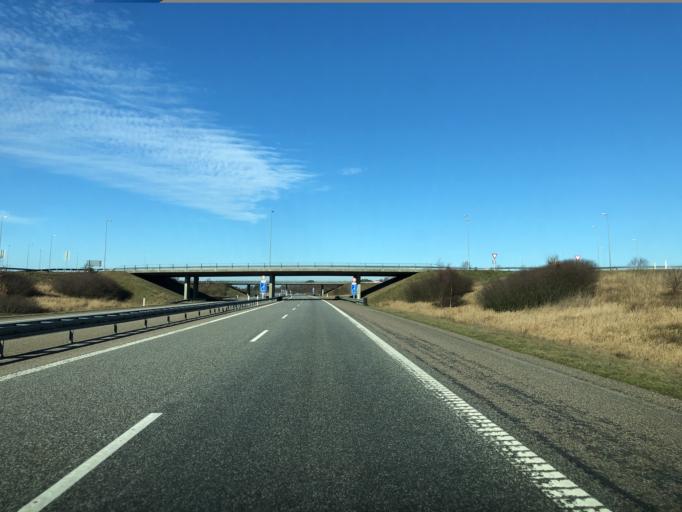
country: DK
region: Central Jutland
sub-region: Herning Kommune
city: Herning
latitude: 56.1537
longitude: 9.0100
